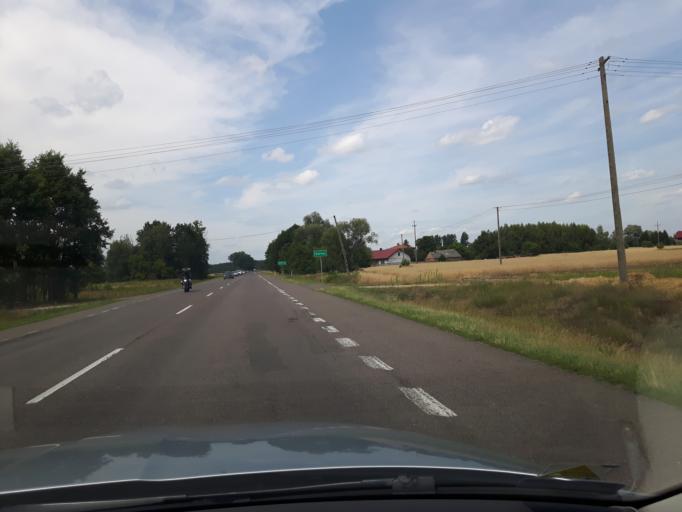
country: PL
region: Masovian Voivodeship
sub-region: Powiat ciechanowski
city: Glinojeck
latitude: 52.7633
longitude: 20.3033
